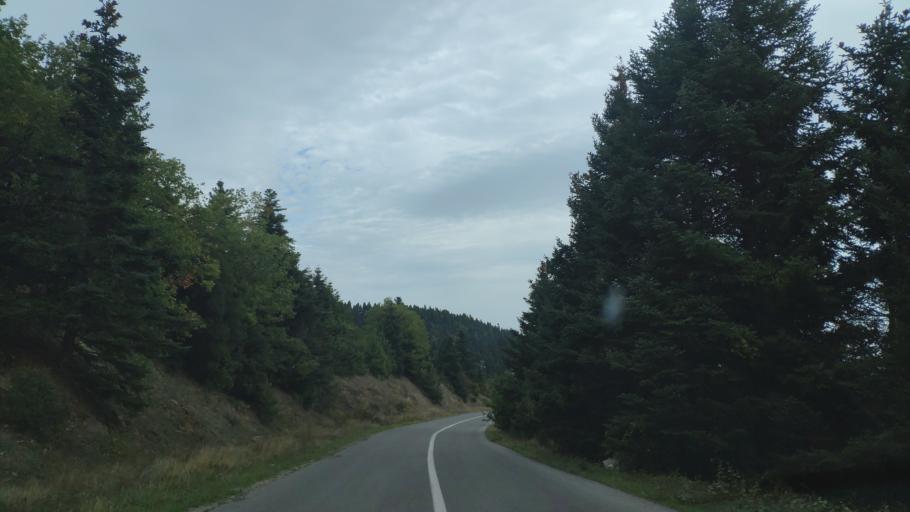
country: GR
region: Central Greece
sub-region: Nomos Fthiotidos
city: Stavros
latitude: 38.7274
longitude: 22.3375
